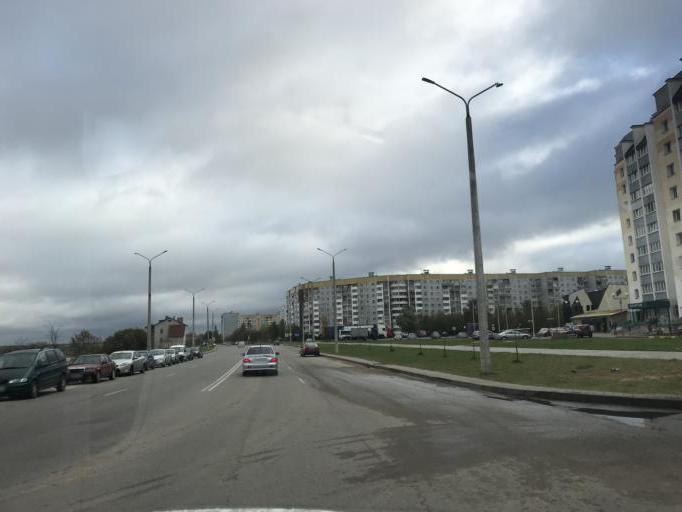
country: BY
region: Mogilev
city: Mahilyow
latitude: 53.8829
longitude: 30.3650
